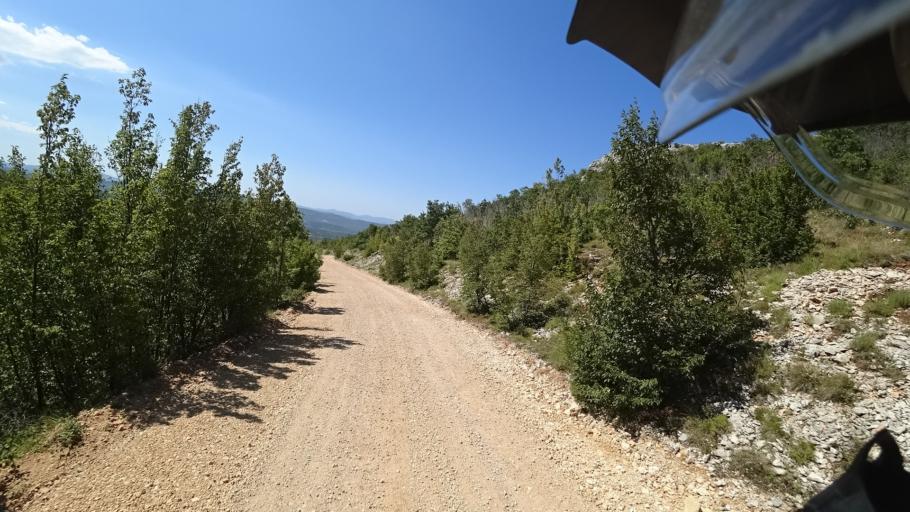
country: HR
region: Splitsko-Dalmatinska
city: Hrvace
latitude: 43.7587
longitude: 16.4651
